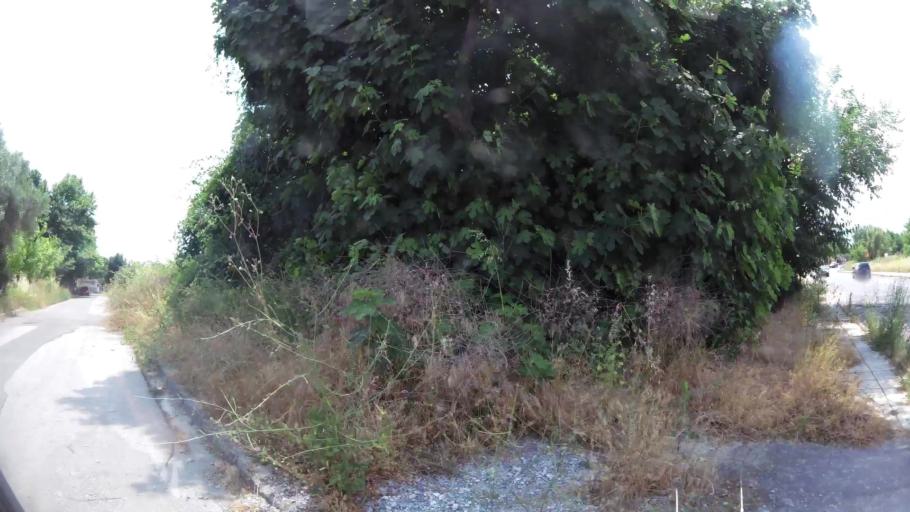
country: GR
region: Central Macedonia
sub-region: Nomos Pierias
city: Peristasi
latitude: 40.2643
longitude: 22.5344
